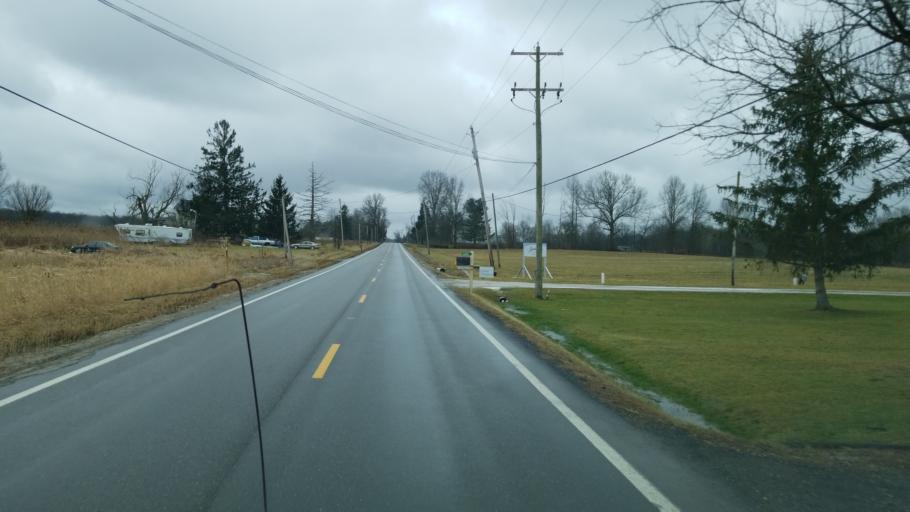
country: US
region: Ohio
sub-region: Trumbull County
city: Champion Heights
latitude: 41.3654
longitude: -80.9546
